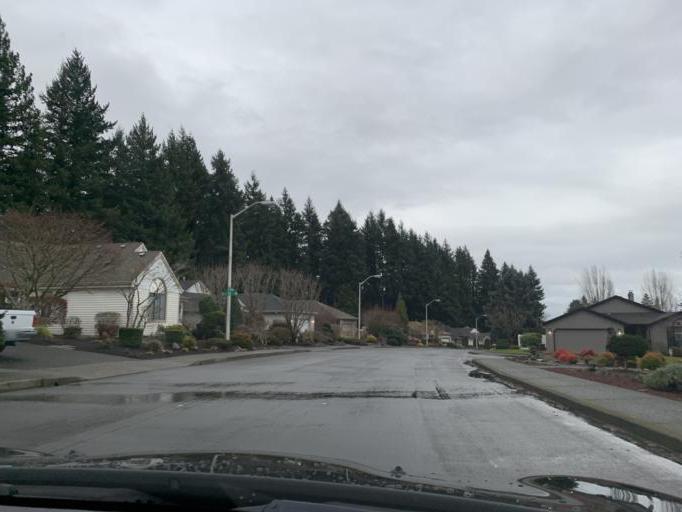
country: US
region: Washington
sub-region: Clark County
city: Mill Plain
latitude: 45.5996
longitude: -122.5111
